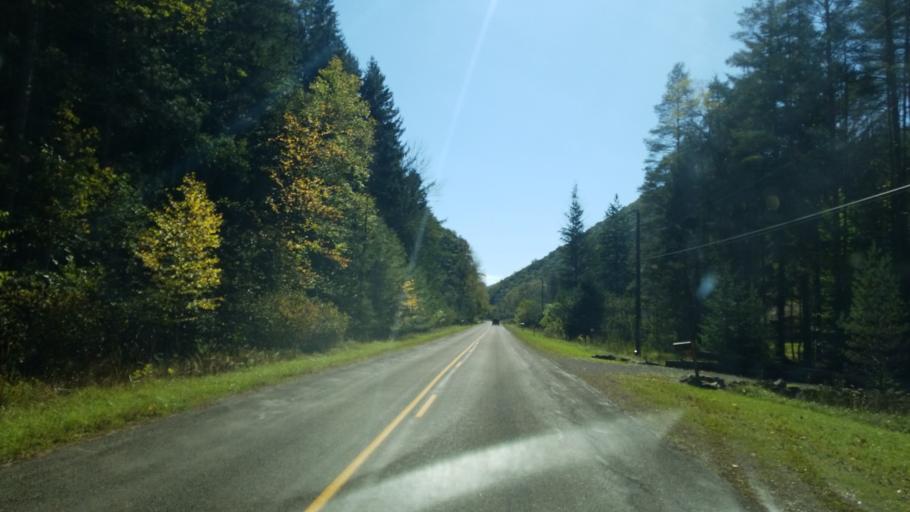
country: US
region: Pennsylvania
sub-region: Elk County
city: Saint Marys
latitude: 41.2795
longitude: -78.3982
